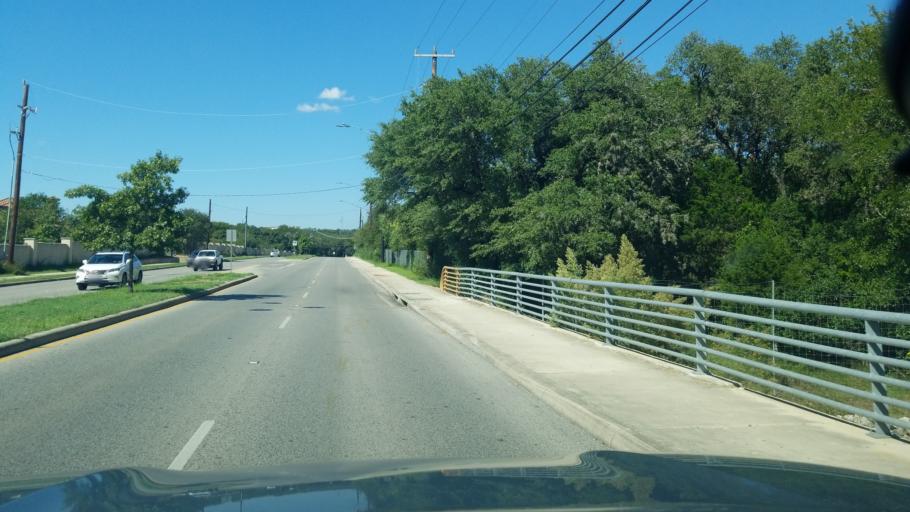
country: US
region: Texas
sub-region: Bexar County
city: Hollywood Park
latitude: 29.5871
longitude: -98.4388
